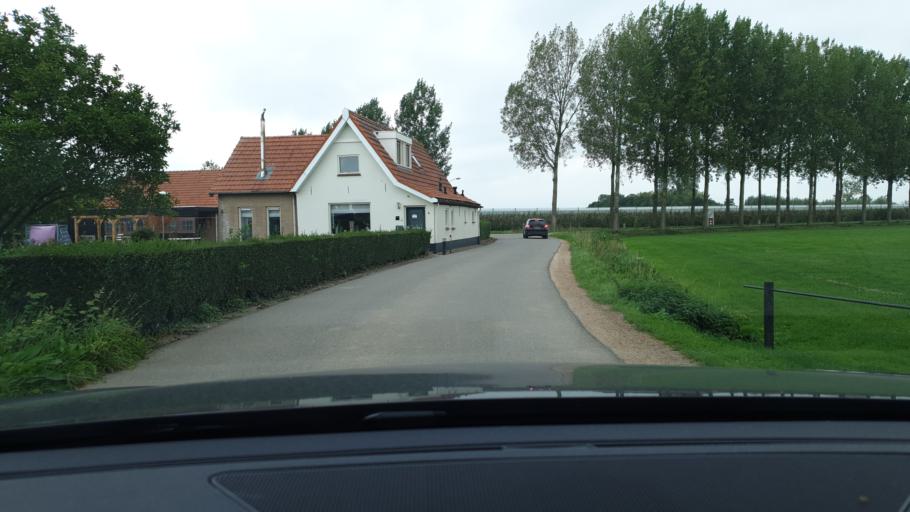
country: NL
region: Gelderland
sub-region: Gemeente Wijchen
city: Bergharen
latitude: 51.8279
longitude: 5.6319
